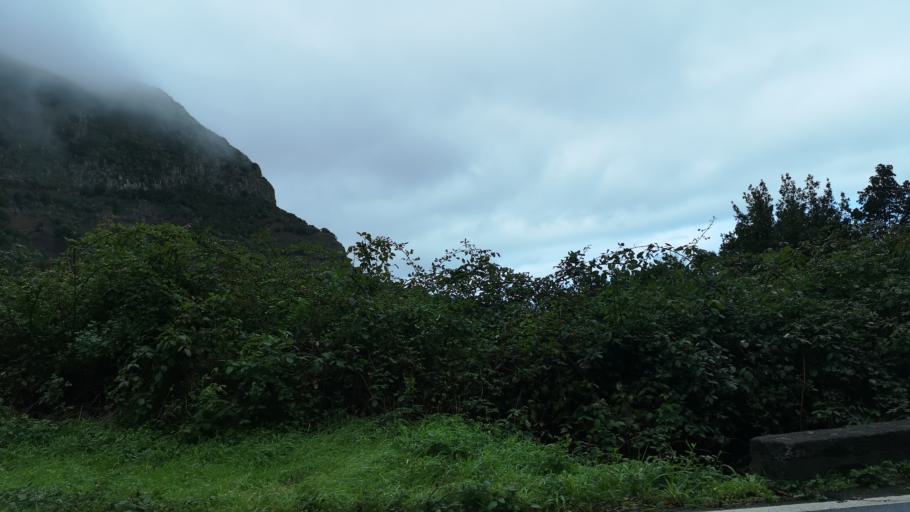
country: ES
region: Canary Islands
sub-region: Provincia de Santa Cruz de Tenerife
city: Hermigua
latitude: 28.1311
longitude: -17.2035
